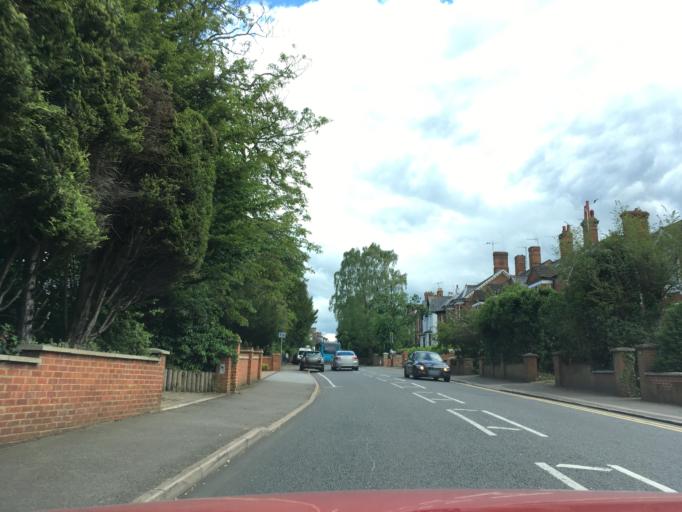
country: GB
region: England
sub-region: Milton Keynes
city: Woburn Sands
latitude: 52.0142
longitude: -0.6487
